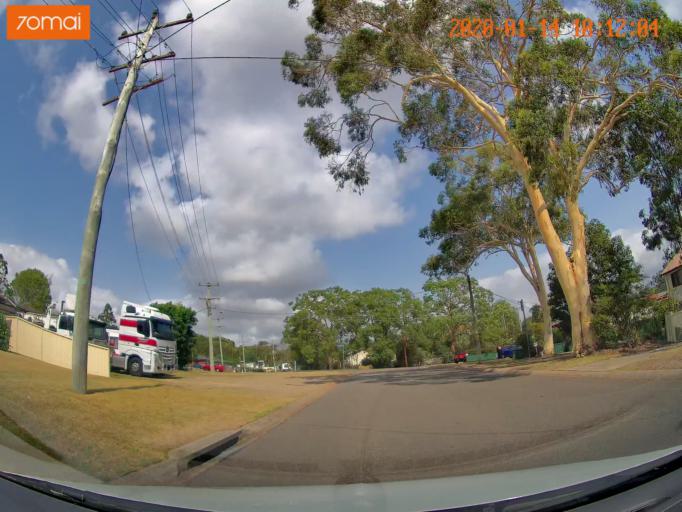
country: AU
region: New South Wales
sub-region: Lake Macquarie Shire
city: Dora Creek
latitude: -33.1177
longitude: 151.5308
